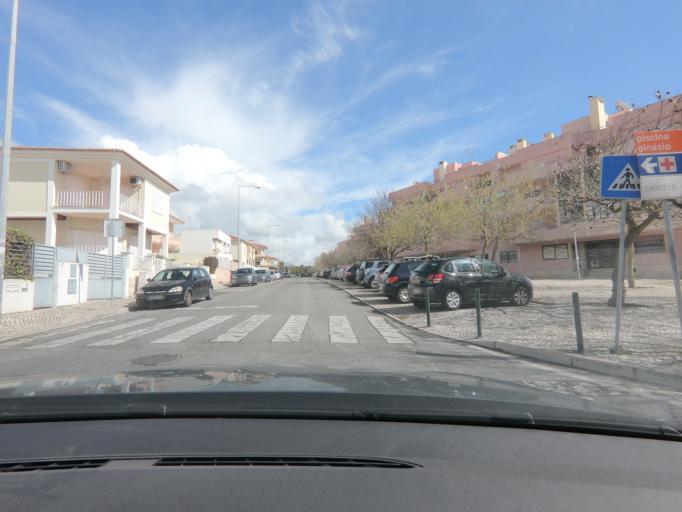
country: PT
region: Lisbon
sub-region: Cascais
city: Sao Domingos de Rana
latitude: 38.6988
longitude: -9.3240
